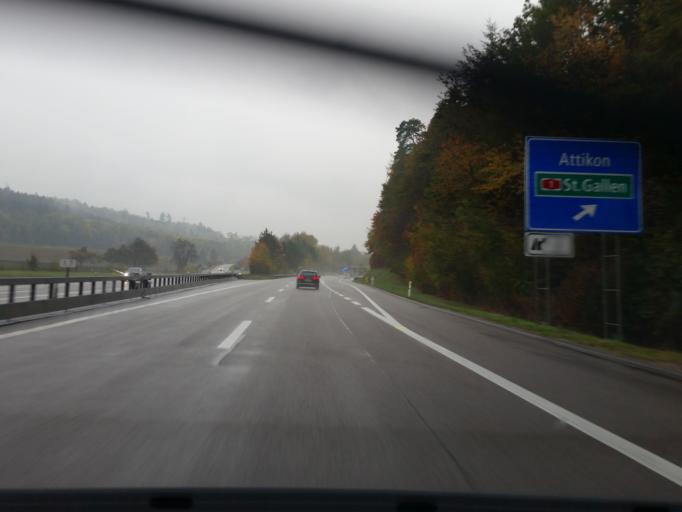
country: CH
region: Zurich
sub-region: Bezirk Winterthur
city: Sulz
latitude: 47.5369
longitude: 8.8066
